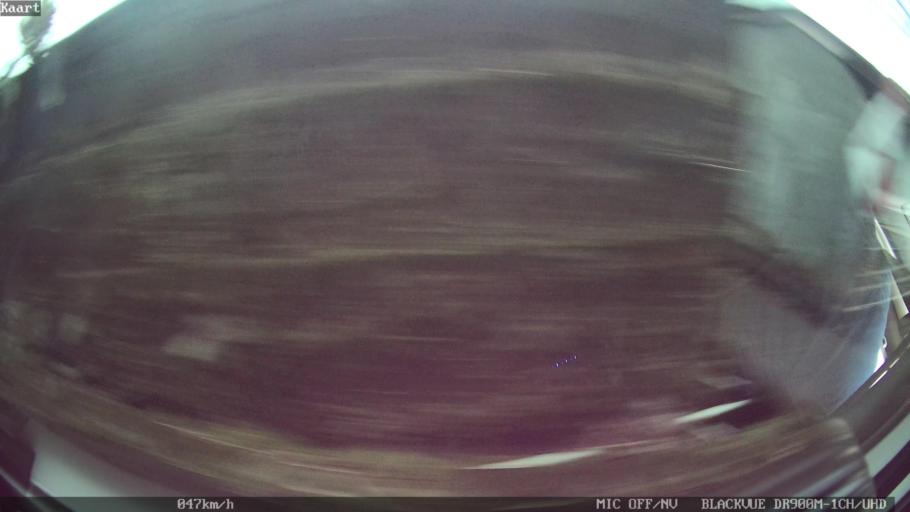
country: ID
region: Bali
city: Peneng
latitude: -8.3466
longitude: 115.1848
